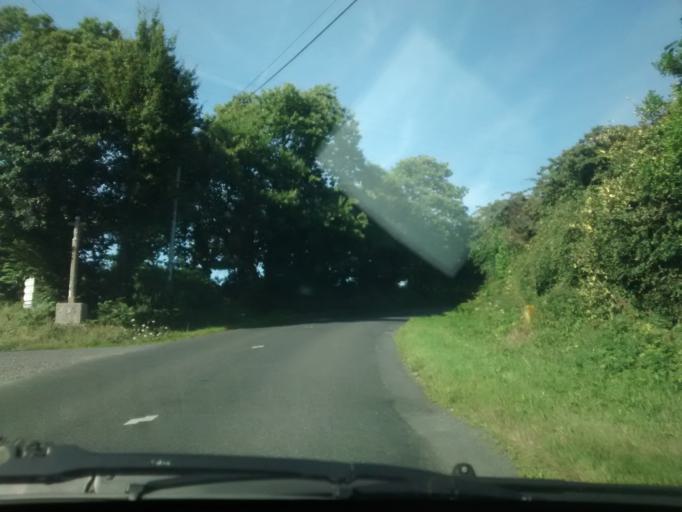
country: FR
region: Brittany
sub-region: Departement des Cotes-d'Armor
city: Lannion
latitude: 48.7436
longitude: -3.4267
